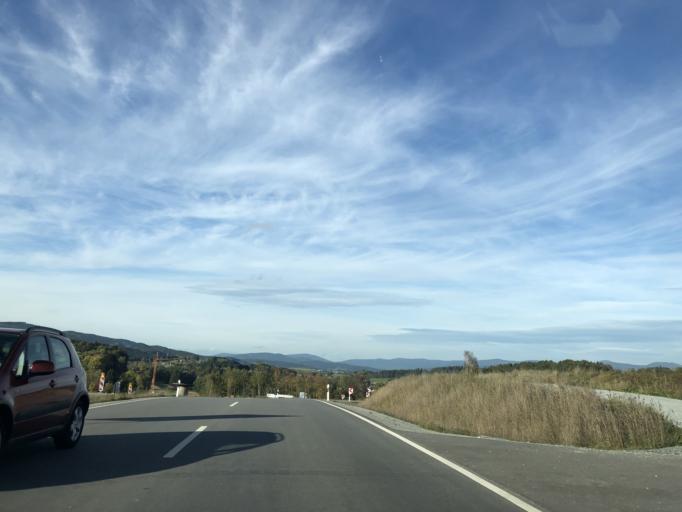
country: DE
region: Bavaria
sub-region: Lower Bavaria
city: Gotteszell
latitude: 48.9473
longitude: 12.9795
